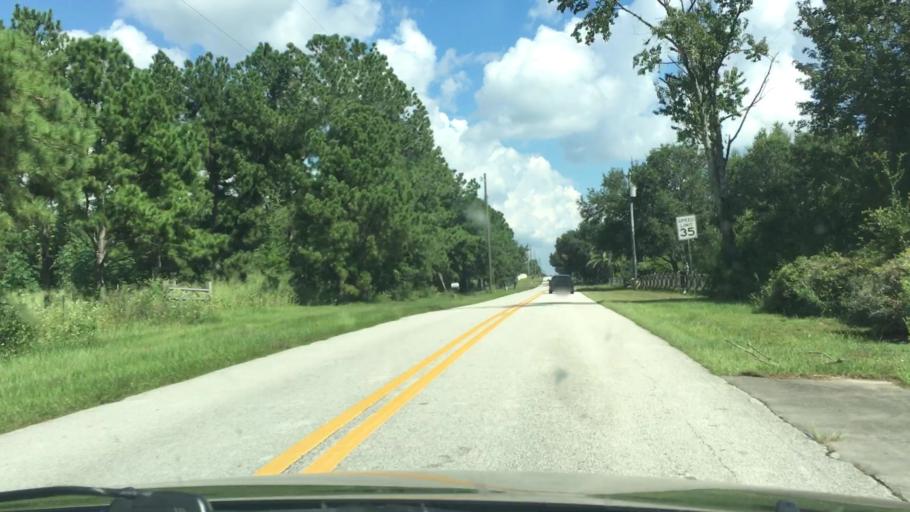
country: US
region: Florida
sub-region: Lake County
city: Montverde
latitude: 28.5972
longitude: -81.6902
